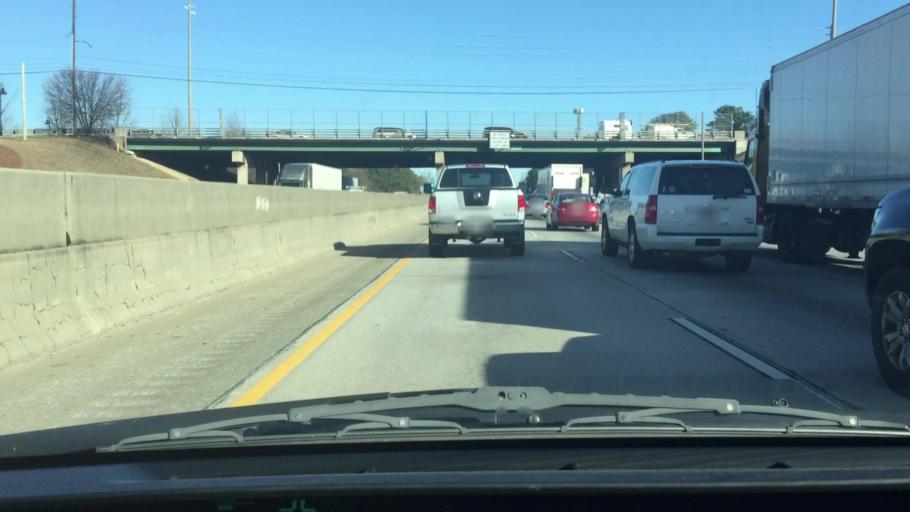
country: US
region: Georgia
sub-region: DeKalb County
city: Tucker
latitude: 33.8455
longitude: -84.2473
